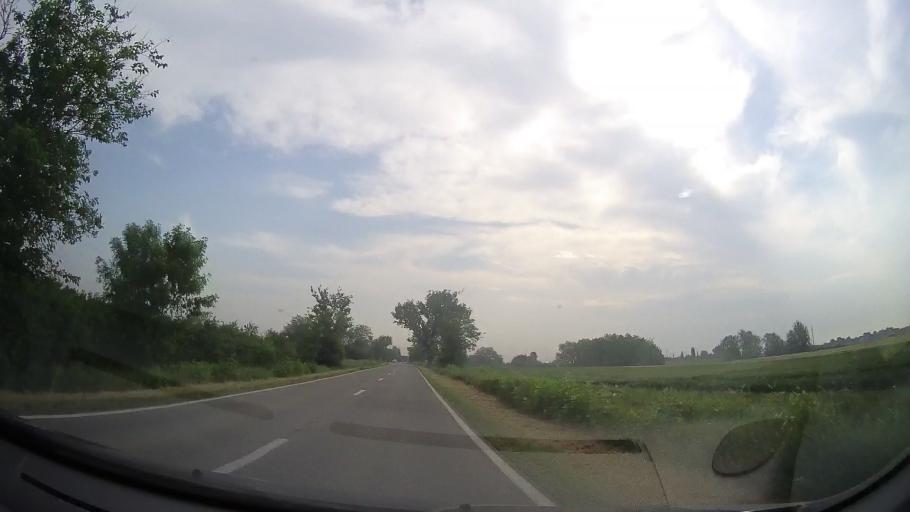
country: RO
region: Timis
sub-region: Comuna Parta
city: Parta
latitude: 45.6425
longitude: 21.1262
